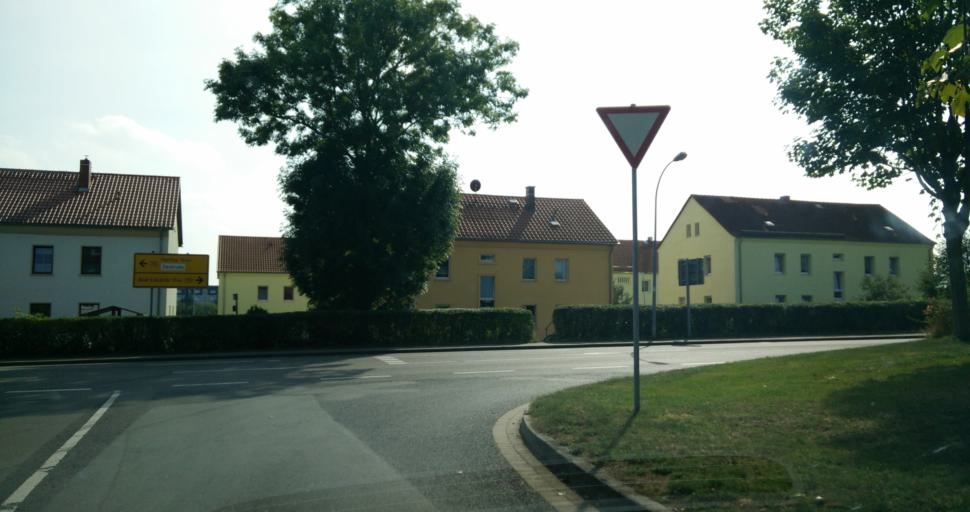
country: DE
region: Saxony
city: Colditz
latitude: 51.1313
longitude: 12.7916
